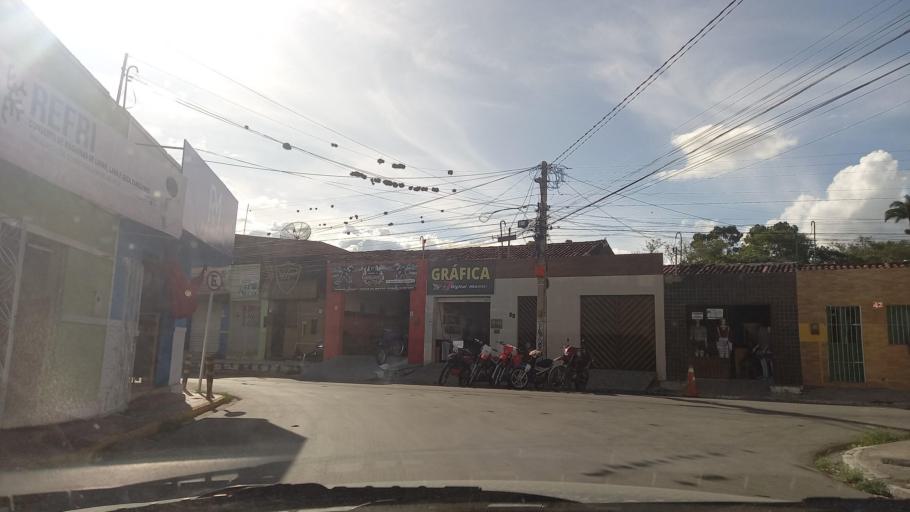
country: BR
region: Pernambuco
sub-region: Gravata
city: Gravata
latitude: -8.2006
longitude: -35.5683
